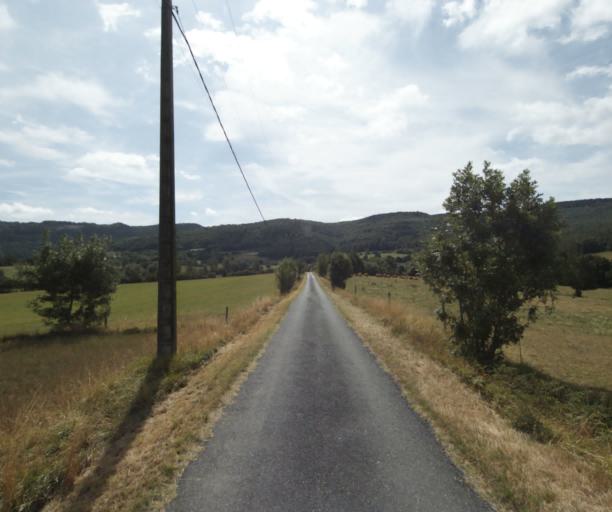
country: FR
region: Midi-Pyrenees
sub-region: Departement du Tarn
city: Dourgne
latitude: 43.4745
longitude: 2.1140
